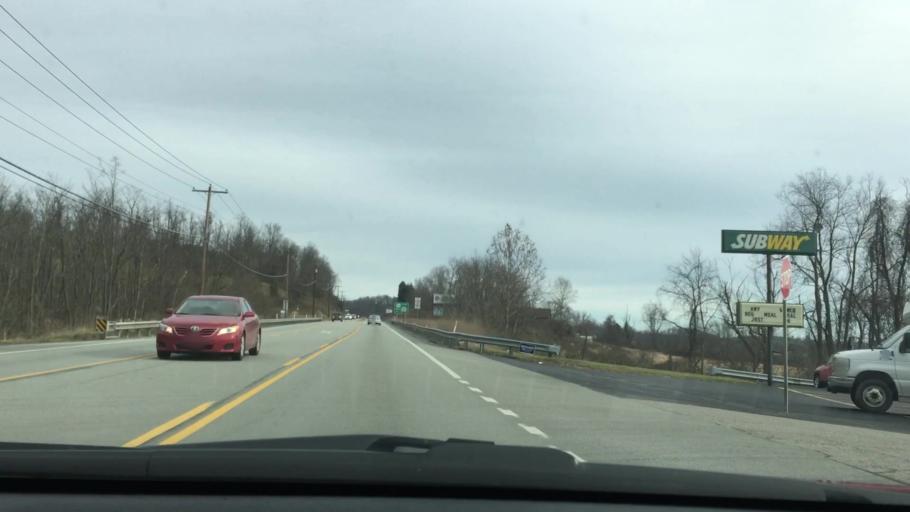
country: US
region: Pennsylvania
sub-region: Fayette County
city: Masontown
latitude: 39.8529
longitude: -79.9122
